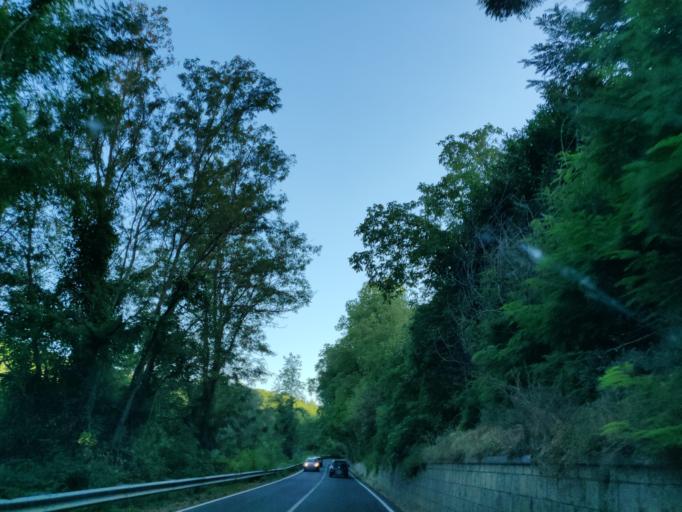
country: IT
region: Latium
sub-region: Provincia di Viterbo
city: Gradoli
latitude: 42.6571
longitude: 11.8478
